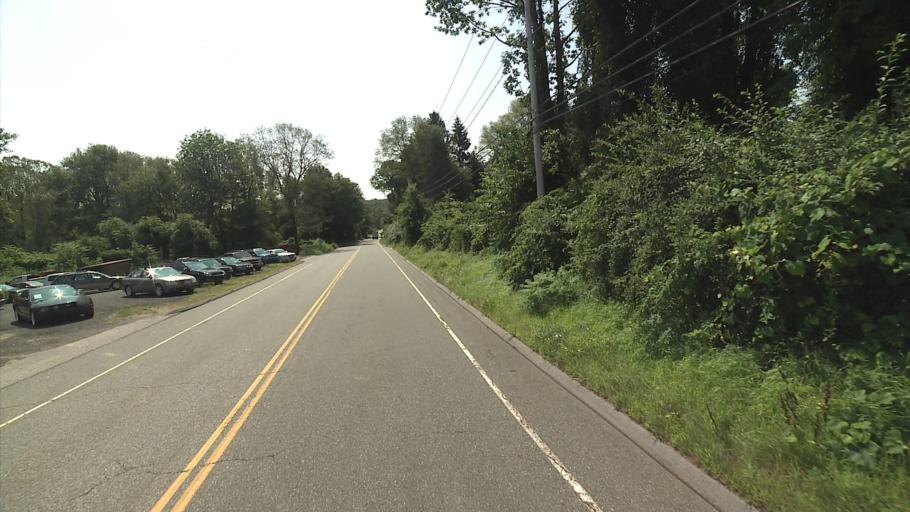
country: US
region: Connecticut
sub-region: New London County
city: Colchester
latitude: 41.5124
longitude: -72.2501
